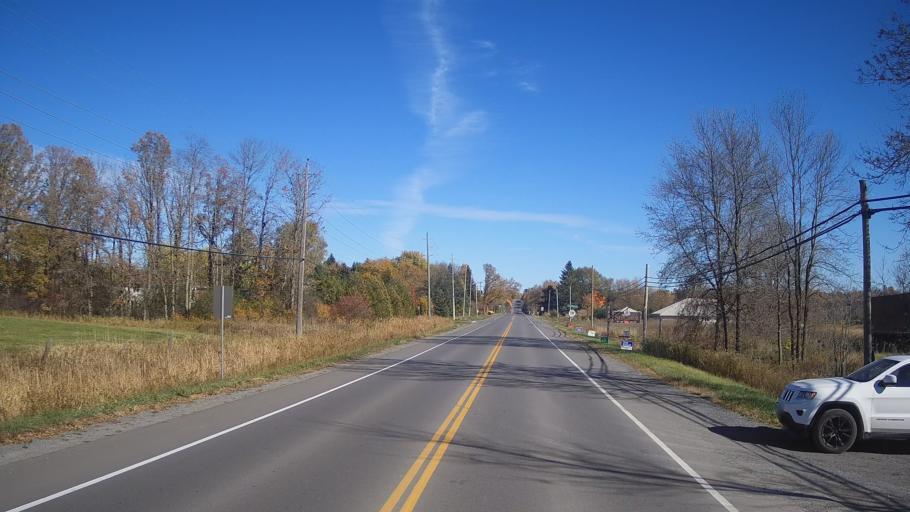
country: CA
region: Ontario
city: Kingston
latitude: 44.4064
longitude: -76.6128
